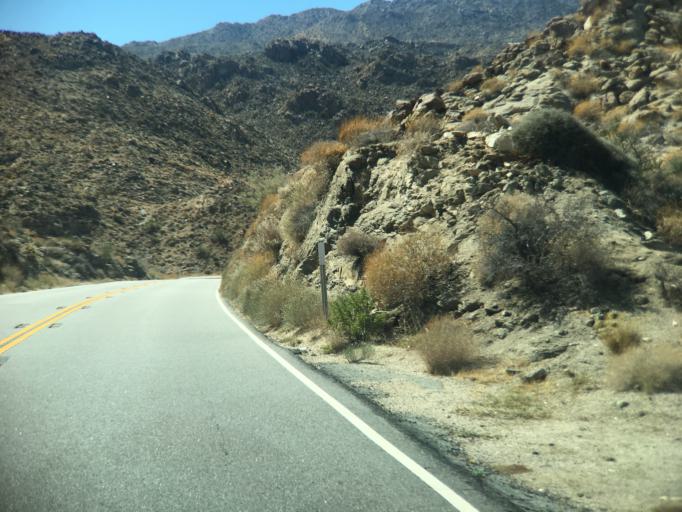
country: US
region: California
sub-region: Riverside County
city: Palm Desert
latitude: 33.6473
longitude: -116.4029
